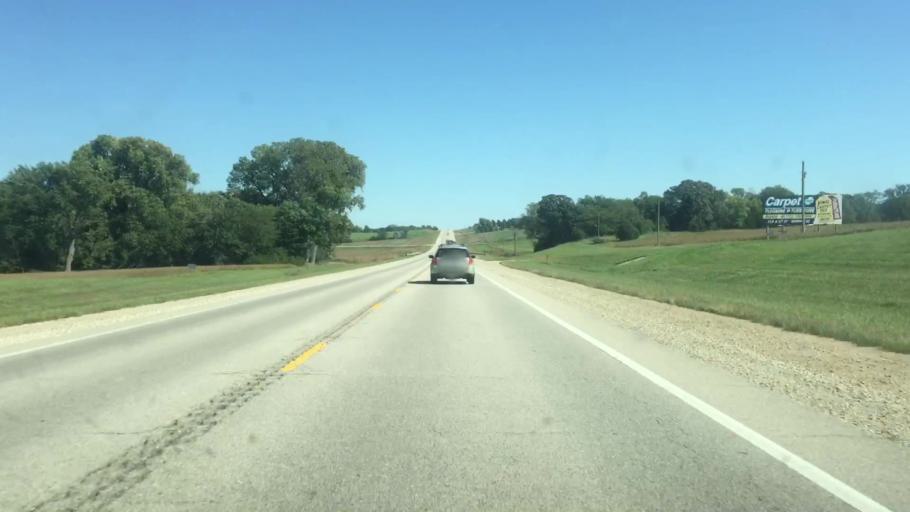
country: US
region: Kansas
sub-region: Nemaha County
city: Seneca
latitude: 39.8412
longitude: -96.0049
